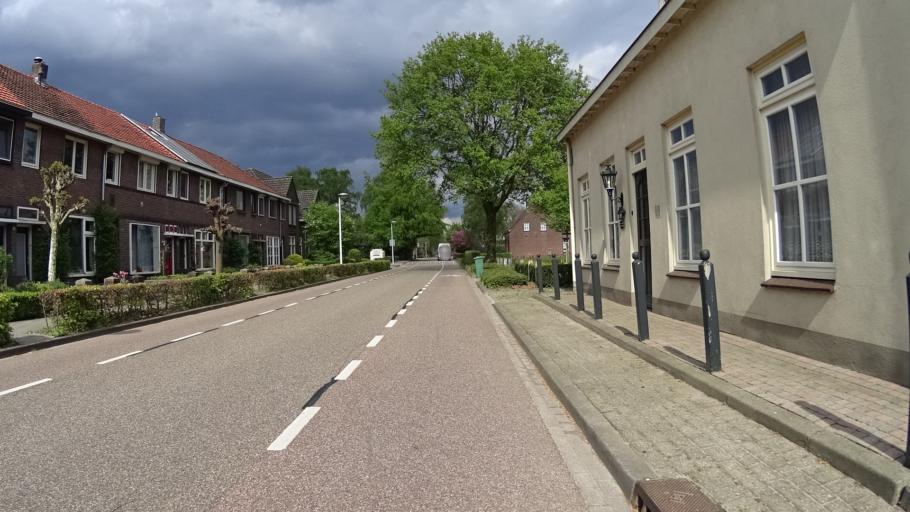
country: NL
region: North Brabant
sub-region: Gemeente Eindhoven
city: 't Hofke
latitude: 51.4606
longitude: 5.5304
